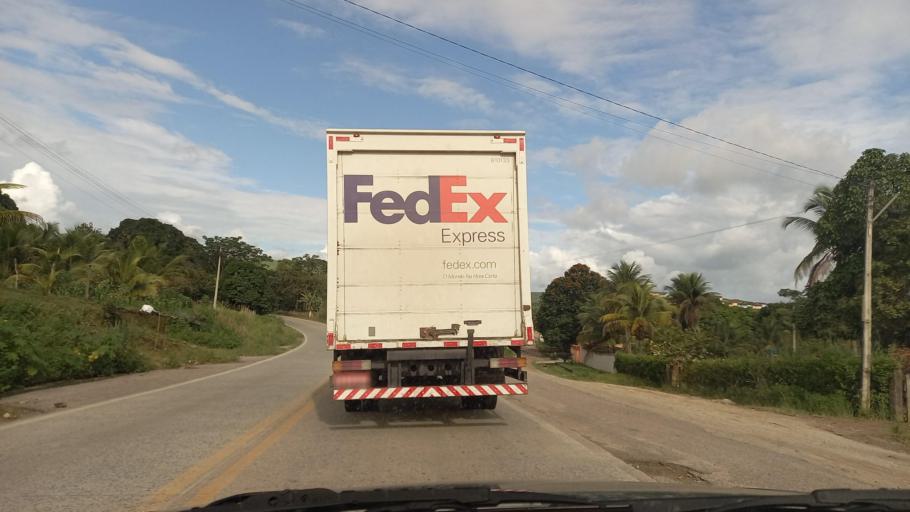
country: BR
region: Pernambuco
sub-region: Catende
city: Catende
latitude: -8.6951
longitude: -35.6658
